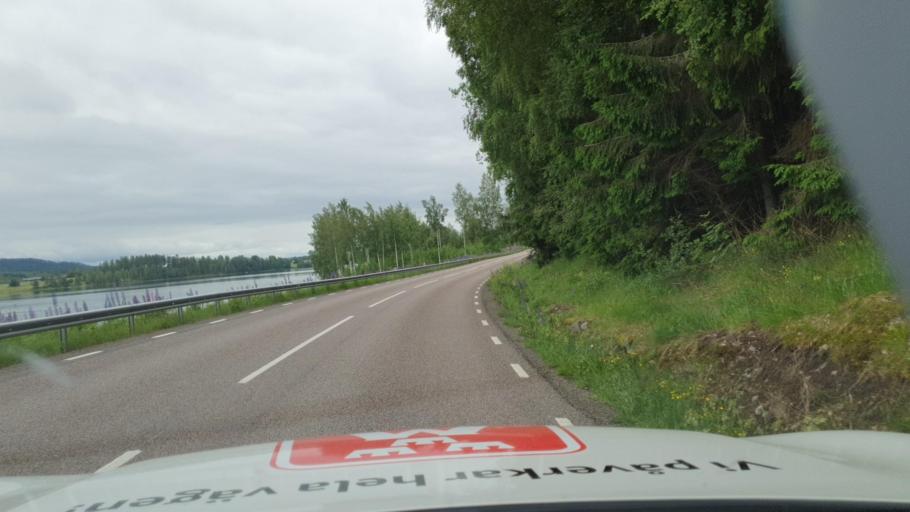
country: SE
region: Vaermland
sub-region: Sunne Kommun
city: Sunne
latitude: 59.8221
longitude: 13.0000
